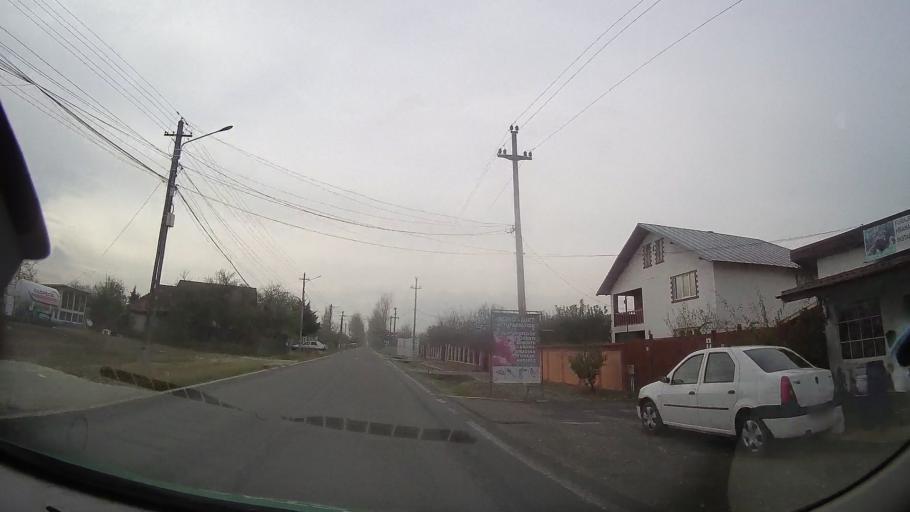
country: RO
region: Ilfov
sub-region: Comuna Gruiu
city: Silistea Snagovului
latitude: 44.7444
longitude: 26.1749
